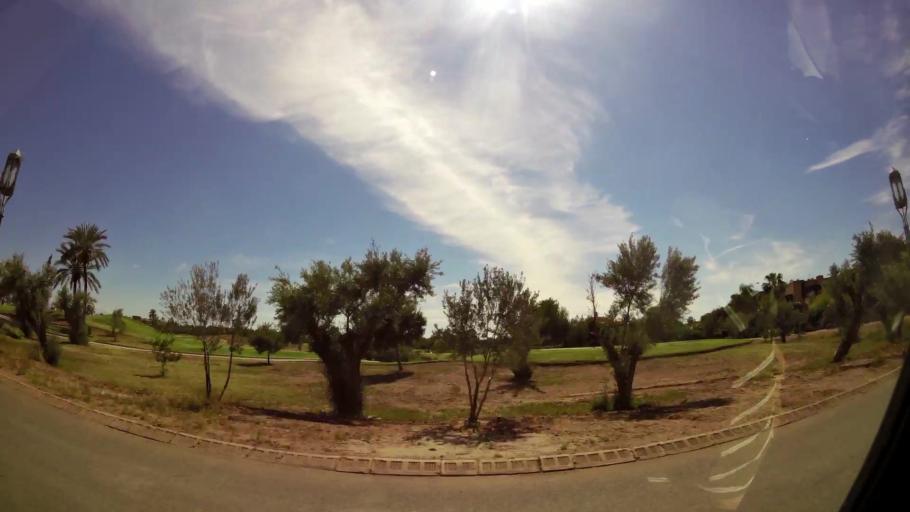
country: MA
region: Marrakech-Tensift-Al Haouz
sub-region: Marrakech
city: Marrakesh
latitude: 31.6195
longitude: -7.9382
